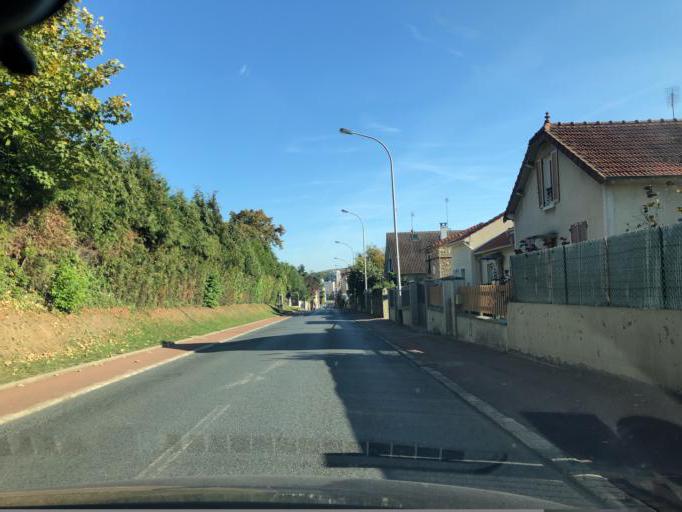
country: FR
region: Ile-de-France
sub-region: Departement des Hauts-de-Seine
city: Chaville
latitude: 48.7961
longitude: 2.1817
